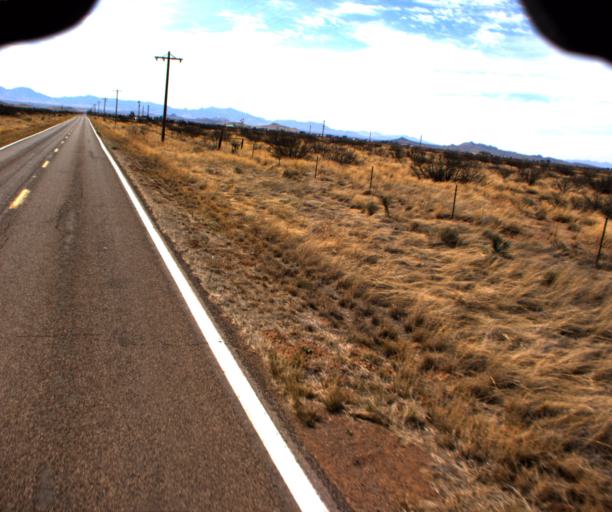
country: US
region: Arizona
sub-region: Cochise County
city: Willcox
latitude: 31.8762
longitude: -109.5945
